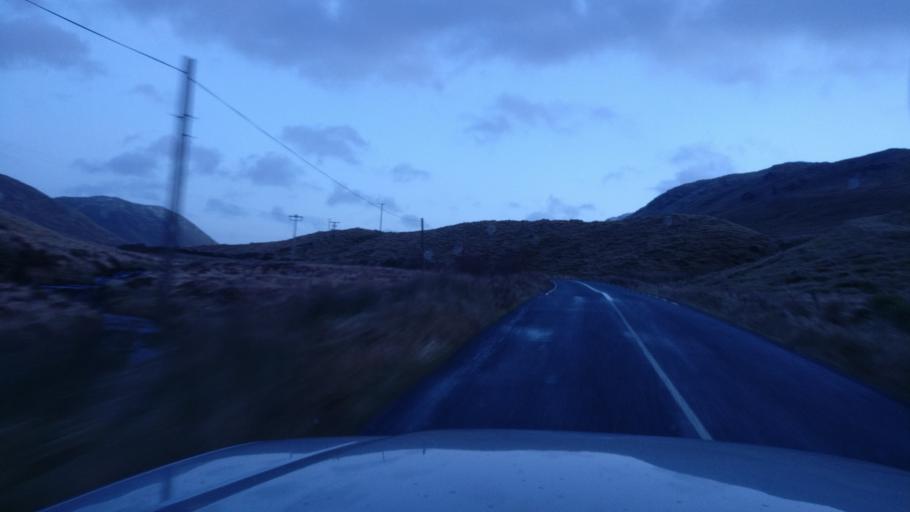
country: IE
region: Connaught
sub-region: Maigh Eo
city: Westport
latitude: 53.5869
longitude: -9.6849
